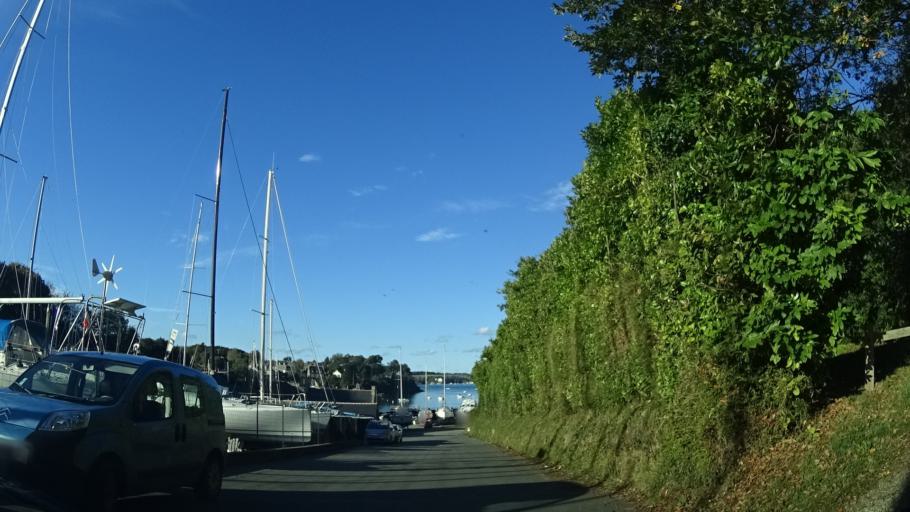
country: FR
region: Brittany
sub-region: Departement d'Ille-et-Vilaine
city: Le Minihic-sur-Rance
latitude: 48.5816
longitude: -2.0004
